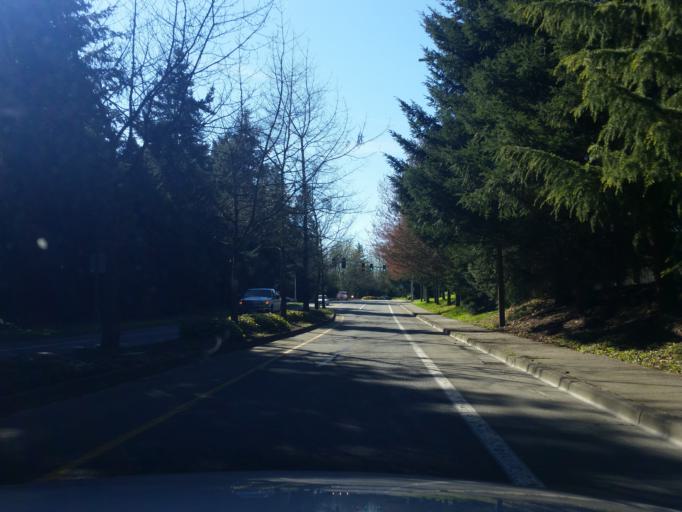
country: US
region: Washington
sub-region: Snohomish County
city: Mill Creek
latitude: 47.8513
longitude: -122.2039
